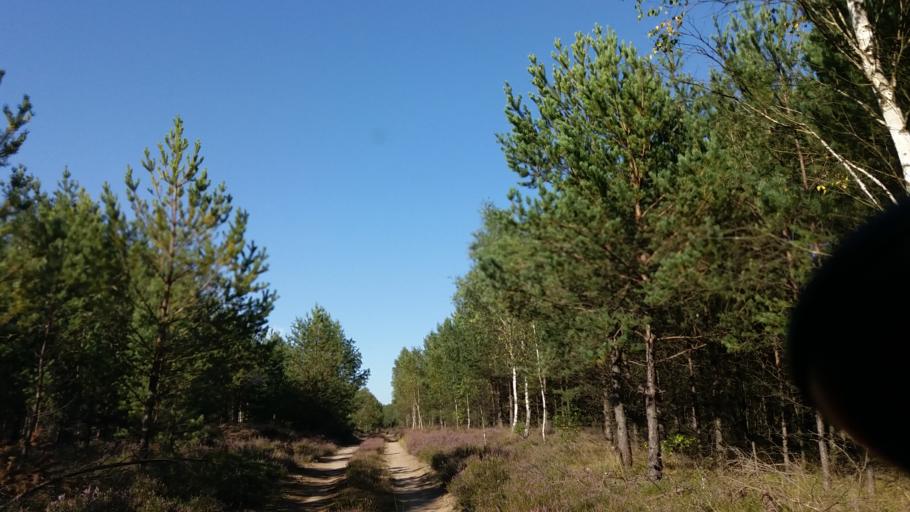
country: PL
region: West Pomeranian Voivodeship
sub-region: Powiat szczecinecki
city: Borne Sulinowo
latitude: 53.5632
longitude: 16.5298
